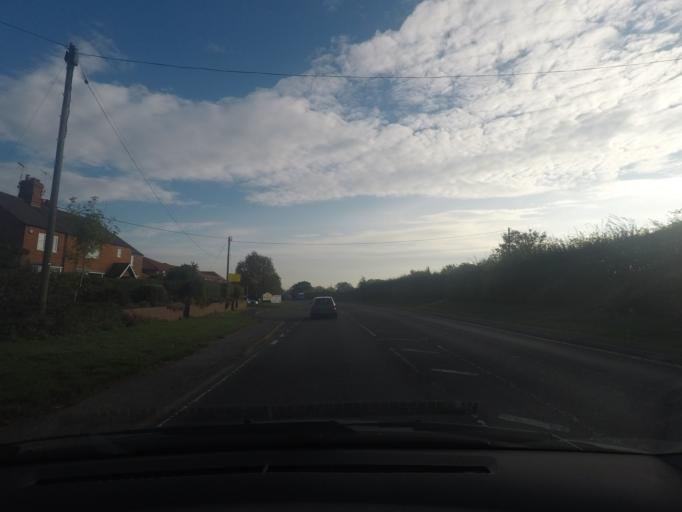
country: GB
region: England
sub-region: City of York
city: Elvington
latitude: 53.9505
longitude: -0.9304
